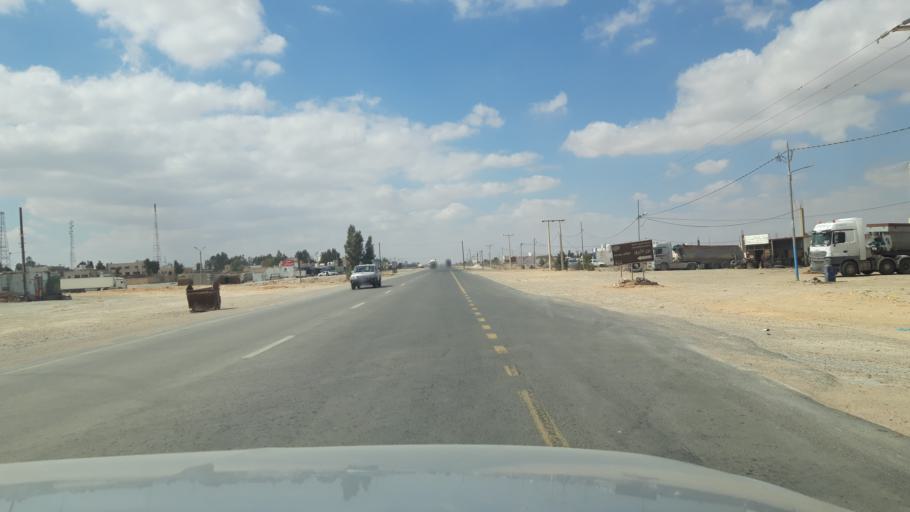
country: JO
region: Amman
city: Al Azraq ash Shamali
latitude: 31.8388
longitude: 36.8100
